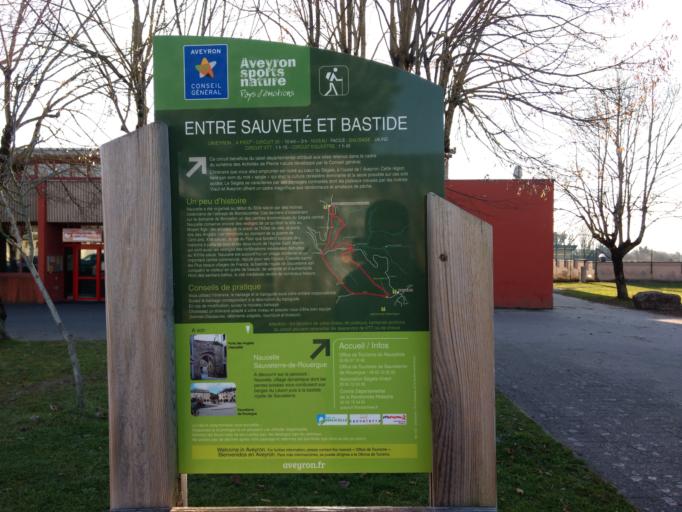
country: FR
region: Midi-Pyrenees
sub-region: Departement de l'Aveyron
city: Naucelle
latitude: 44.1991
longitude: 2.3370
